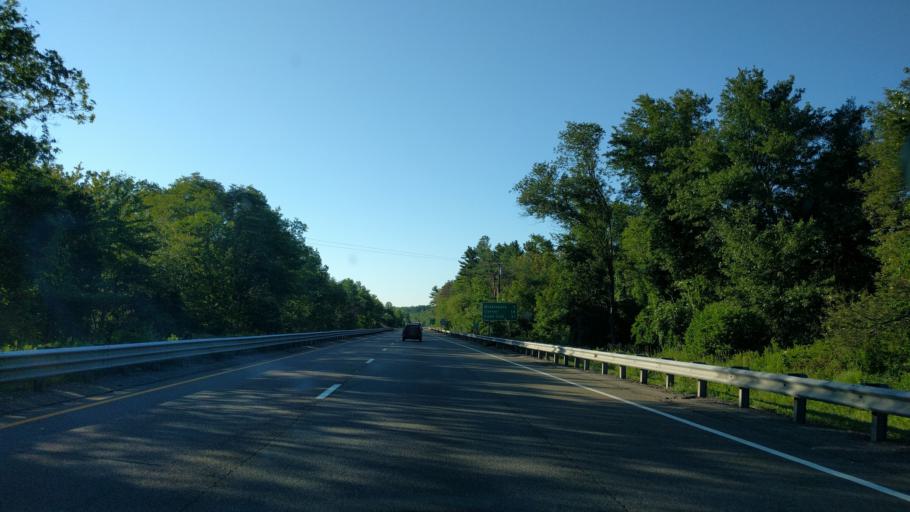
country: US
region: Massachusetts
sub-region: Bristol County
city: Raynham Center
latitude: 41.9291
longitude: -71.0036
